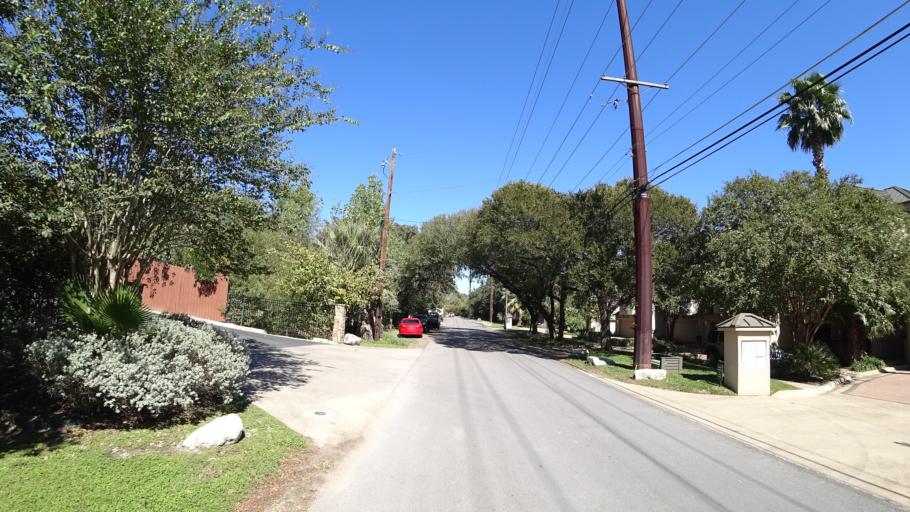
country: US
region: Texas
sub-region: Travis County
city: West Lake Hills
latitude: 30.3035
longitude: -97.7842
